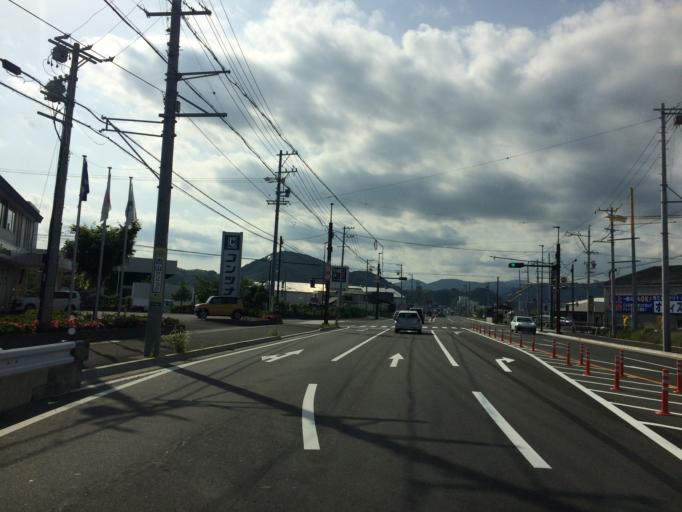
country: JP
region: Shizuoka
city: Fujieda
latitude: 34.8885
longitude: 138.2899
